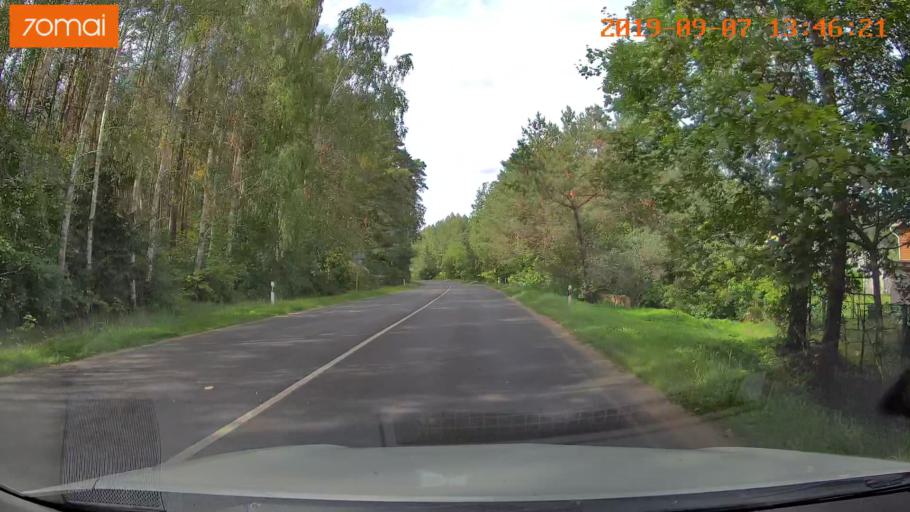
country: LT
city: Baltoji Voke
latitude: 54.5905
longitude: 25.2338
